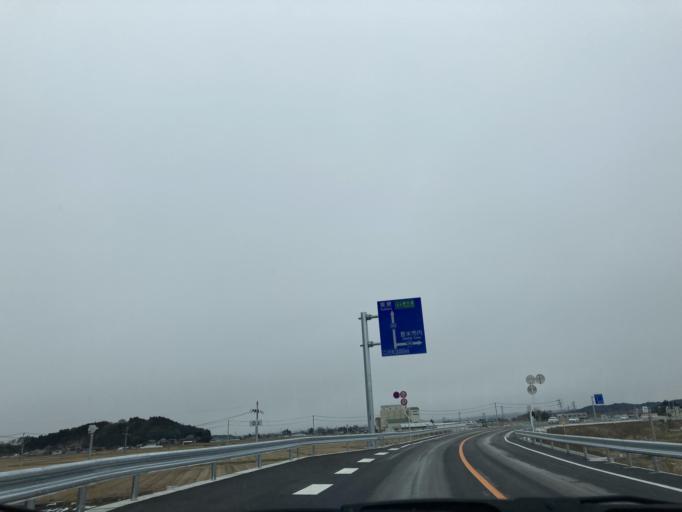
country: JP
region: Miyagi
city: Wakuya
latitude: 38.7042
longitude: 141.1811
